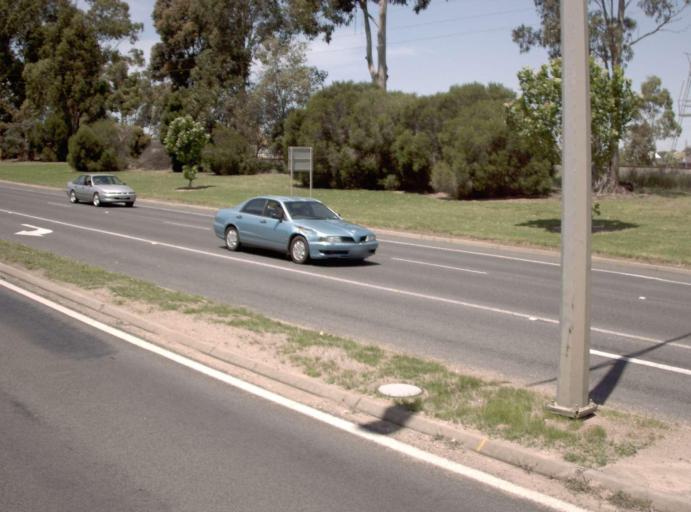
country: AU
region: Victoria
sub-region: Latrobe
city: Traralgon
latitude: -38.2042
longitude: 146.5147
